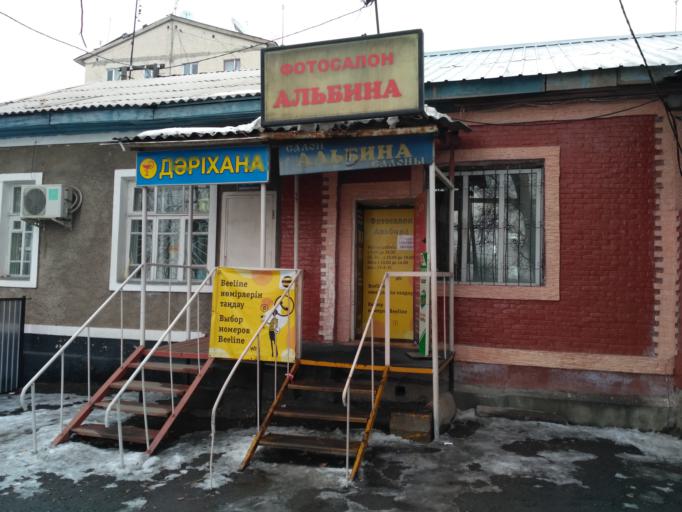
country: KZ
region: Almaty Oblysy
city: Burunday
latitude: 43.1587
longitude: 76.4138
